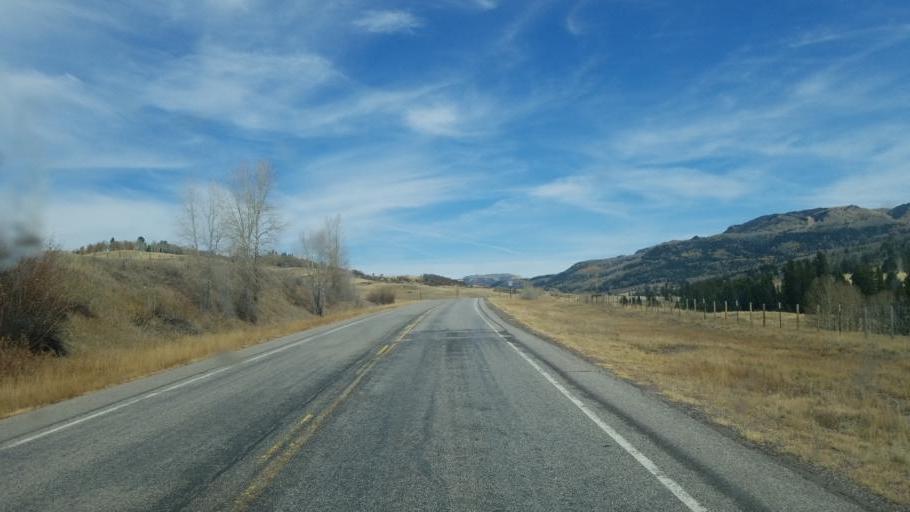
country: US
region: New Mexico
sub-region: Rio Arriba County
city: Chama
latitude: 36.9600
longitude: -106.5292
